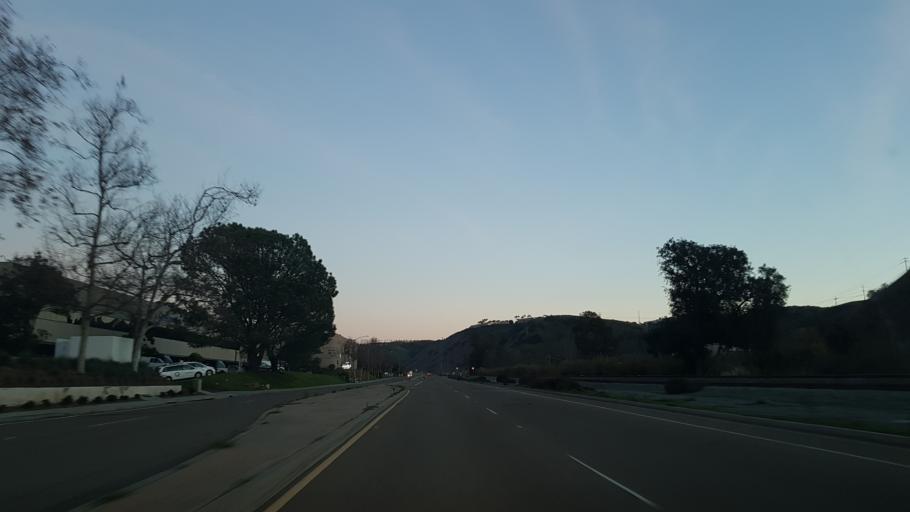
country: US
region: California
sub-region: San Diego County
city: La Jolla
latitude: 32.8979
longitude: -117.2201
